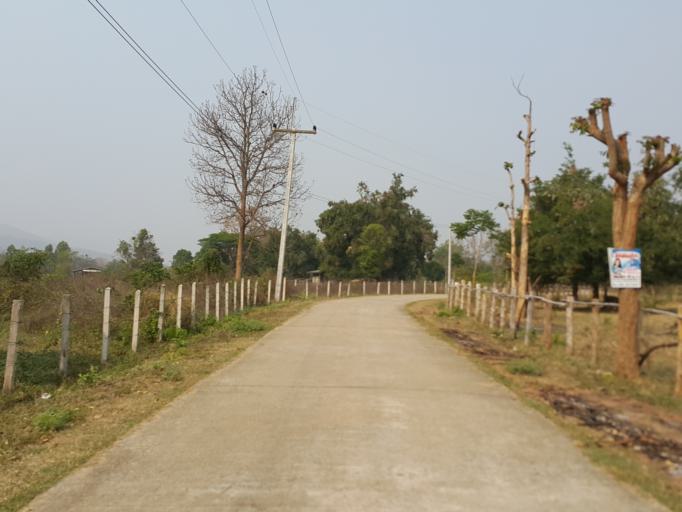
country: TH
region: Lampang
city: Mae Phrik
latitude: 17.4882
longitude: 99.0887
